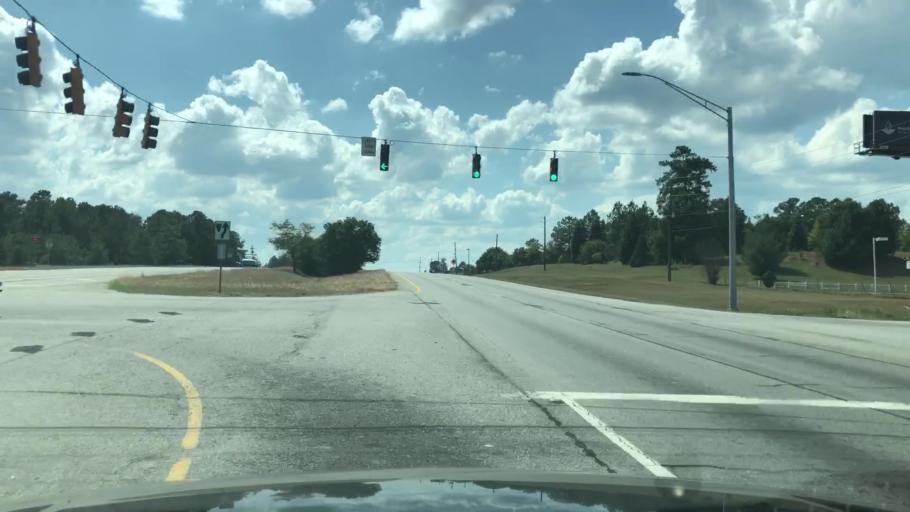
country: US
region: Georgia
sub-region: Bibb County
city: West Point
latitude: 32.8091
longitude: -83.7286
